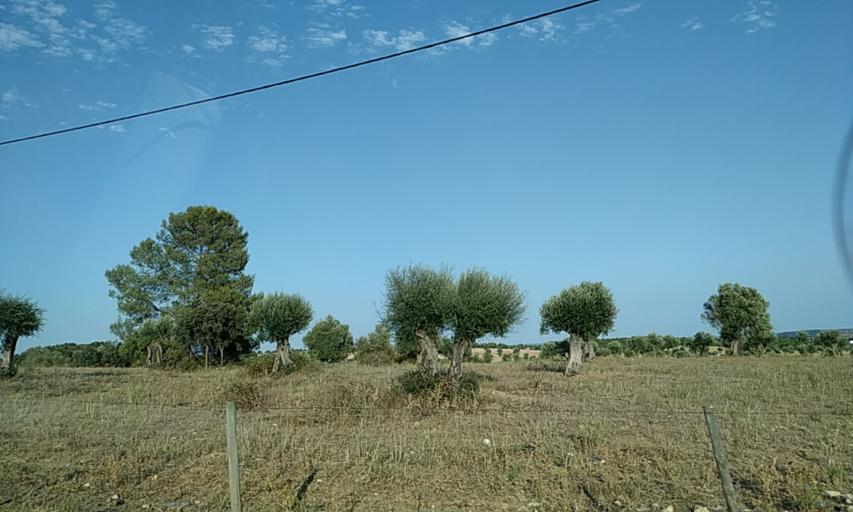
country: PT
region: Santarem
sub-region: Alcanena
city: Alcanena
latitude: 39.3876
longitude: -8.6506
